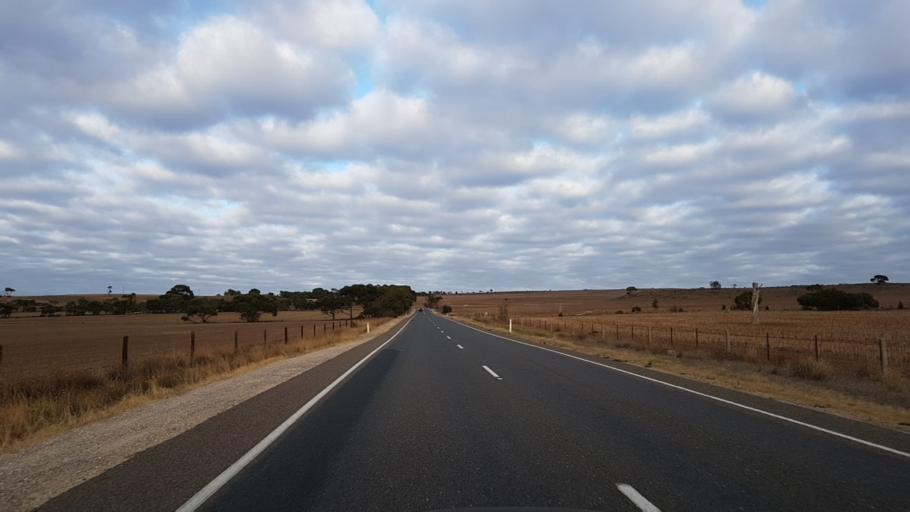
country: AU
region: South Australia
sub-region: Mount Barker
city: Callington
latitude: -35.1810
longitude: 139.0086
